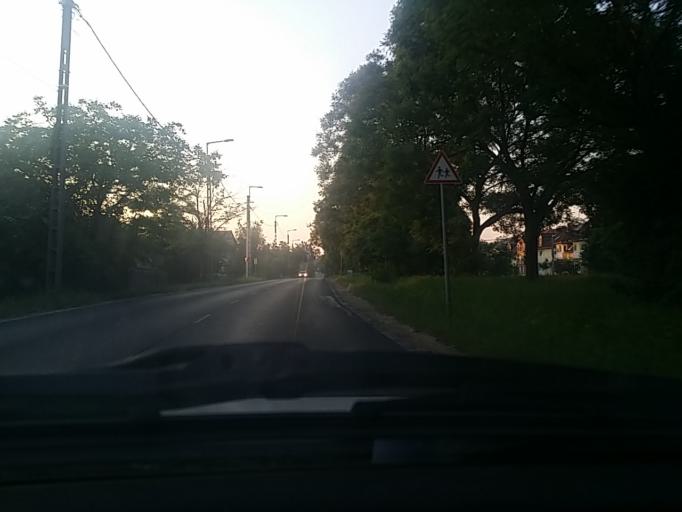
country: HU
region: Budapest
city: Budapest XVII. keruelet
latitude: 47.4712
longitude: 19.2875
